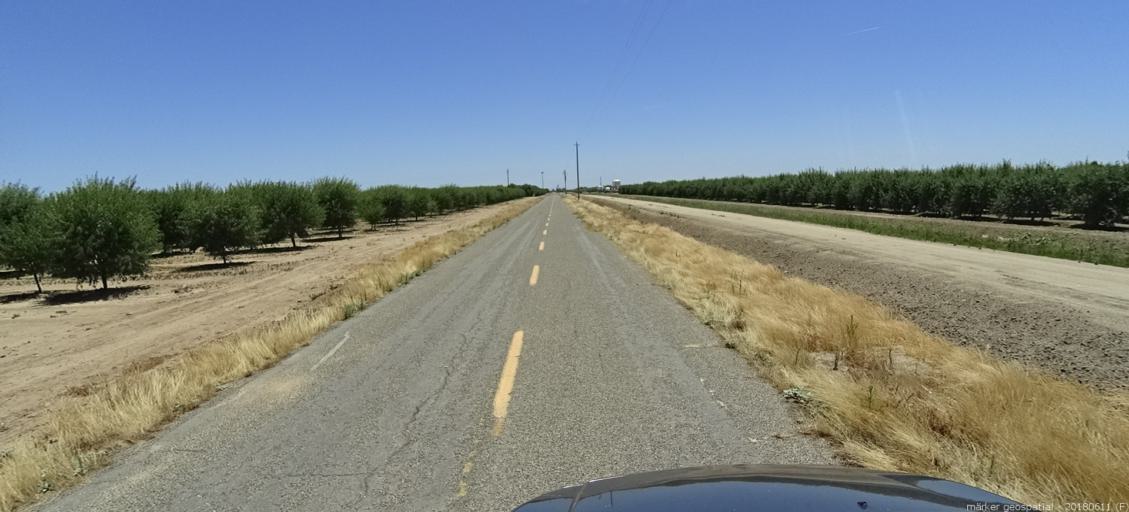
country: US
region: California
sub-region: Madera County
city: Fairmead
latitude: 37.0351
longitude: -120.2114
